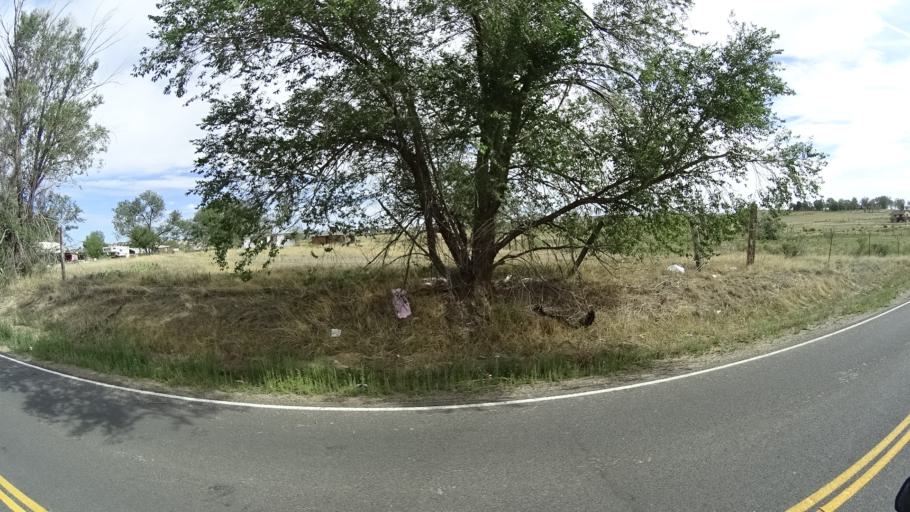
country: US
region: Colorado
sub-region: El Paso County
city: Fountain
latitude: 38.7084
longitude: -104.6819
